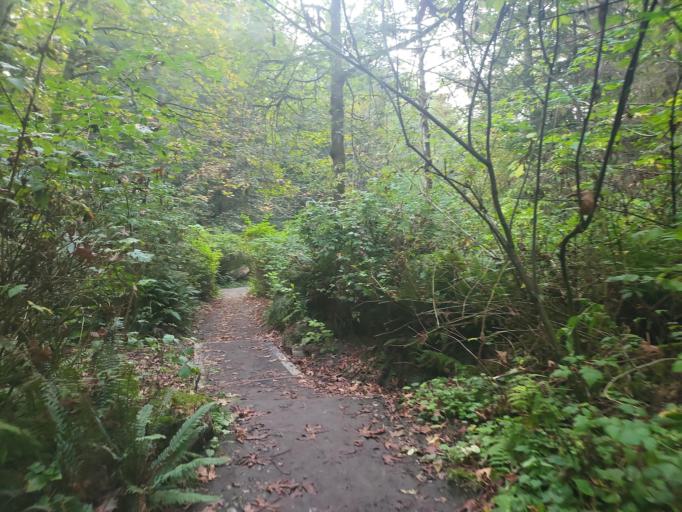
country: US
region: Washington
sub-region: Pierce County
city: Tacoma
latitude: 47.3148
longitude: -122.4131
